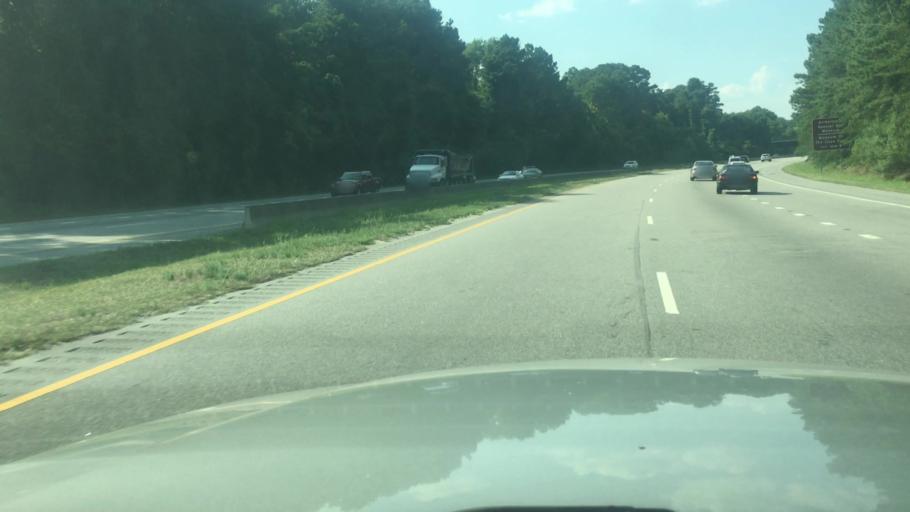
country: US
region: North Carolina
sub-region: Cumberland County
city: Fayetteville
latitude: 35.0483
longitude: -78.8939
